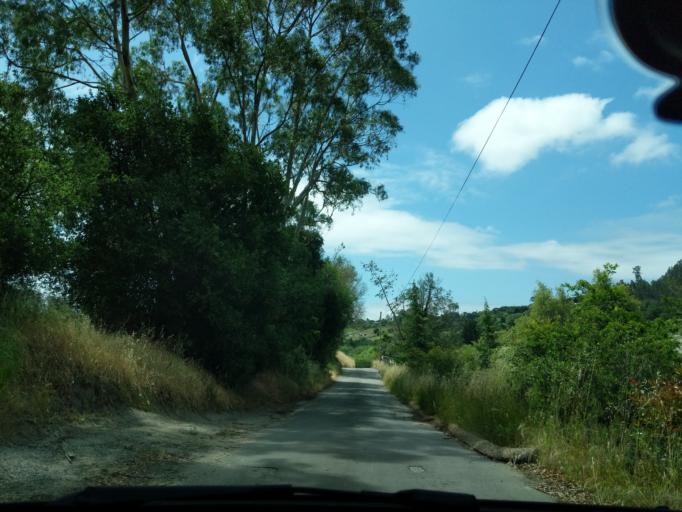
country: US
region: California
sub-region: Santa Cruz County
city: Aptos Hills-Larkin Valley
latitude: 36.9398
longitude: -121.8085
